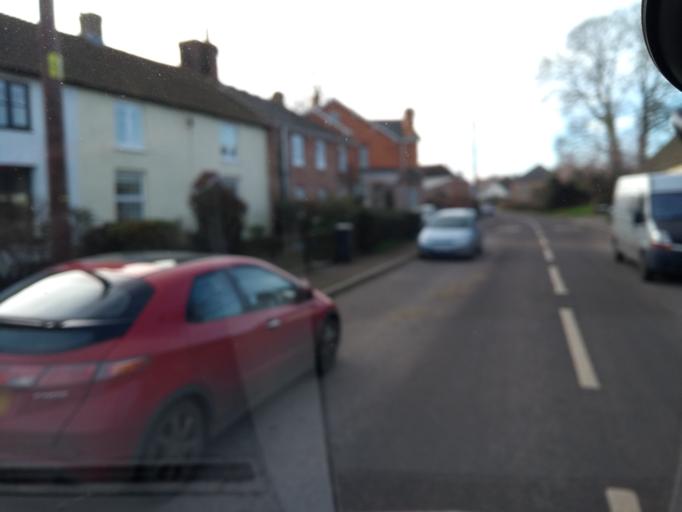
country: GB
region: England
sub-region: Somerset
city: Creech Saint Michael
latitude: 51.0223
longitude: -2.9722
